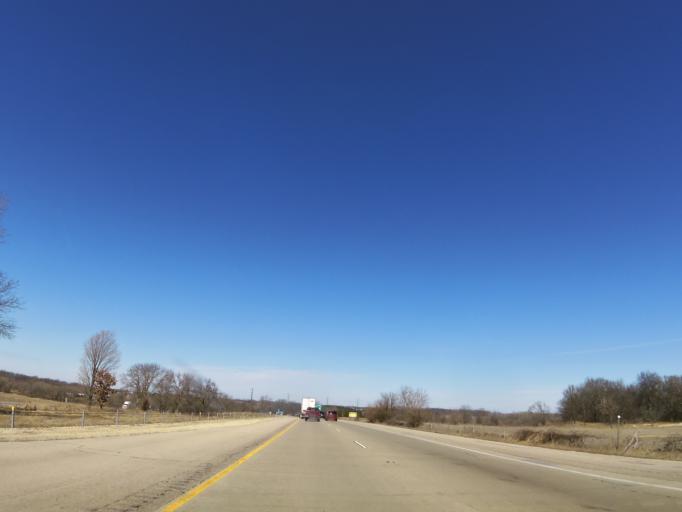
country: US
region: Wisconsin
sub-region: Rock County
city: Edgerton
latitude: 42.8555
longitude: -89.0362
